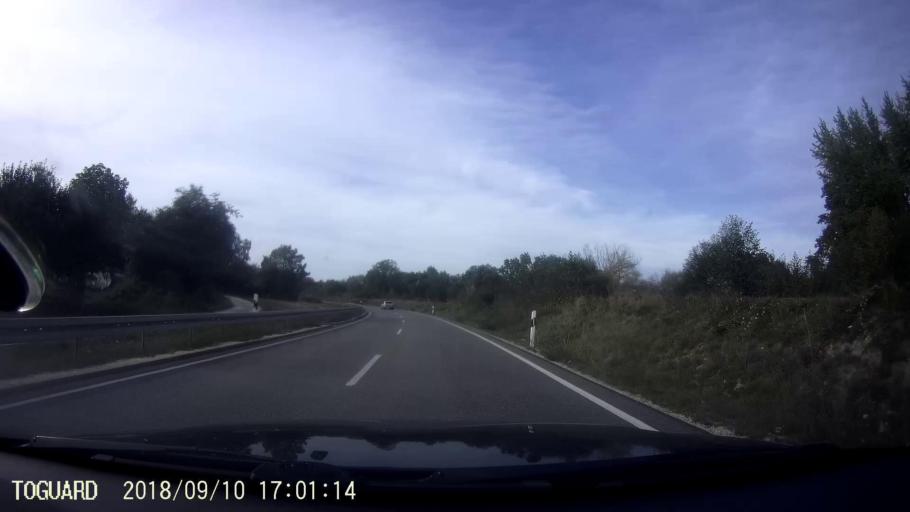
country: CH
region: Thurgau
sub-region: Kreuzlingen District
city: Gottlieben
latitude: 47.6928
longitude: 9.1365
